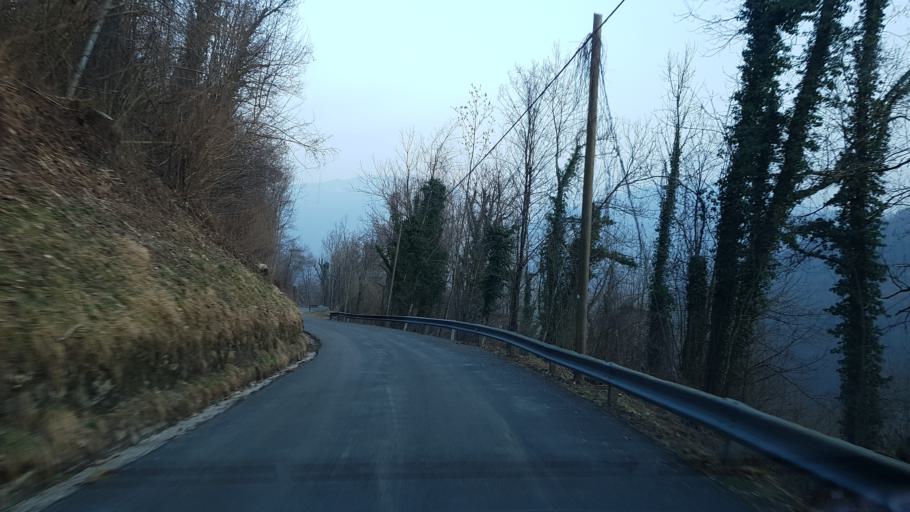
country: IT
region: Friuli Venezia Giulia
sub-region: Provincia di Udine
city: Taipana
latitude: 46.2388
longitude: 13.3952
